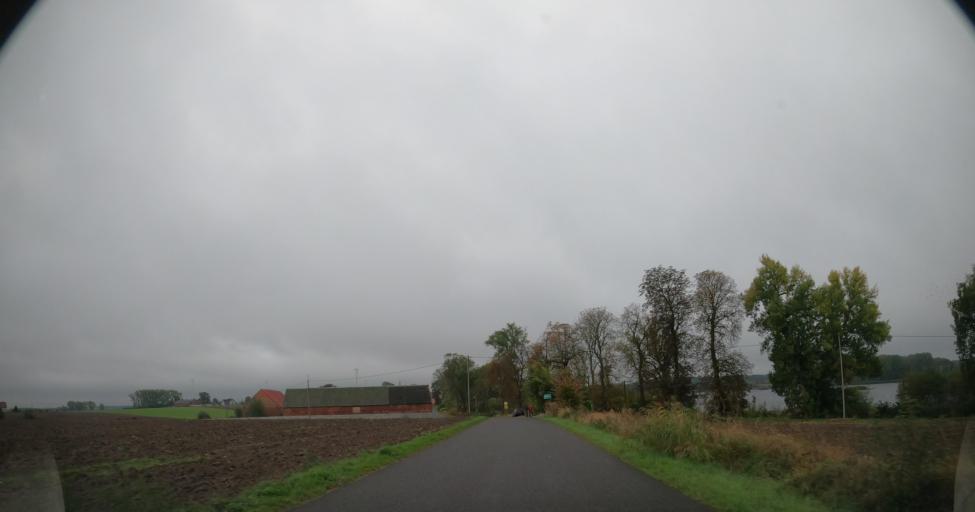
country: PL
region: West Pomeranian Voivodeship
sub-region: Powiat pyrzycki
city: Kozielice
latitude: 53.0981
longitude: 14.7667
